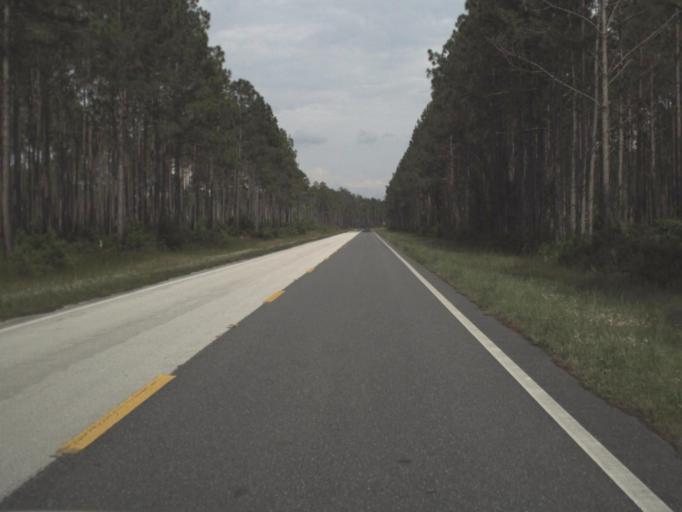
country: US
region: Florida
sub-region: Baker County
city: Macclenny
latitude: 30.5665
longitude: -82.4059
